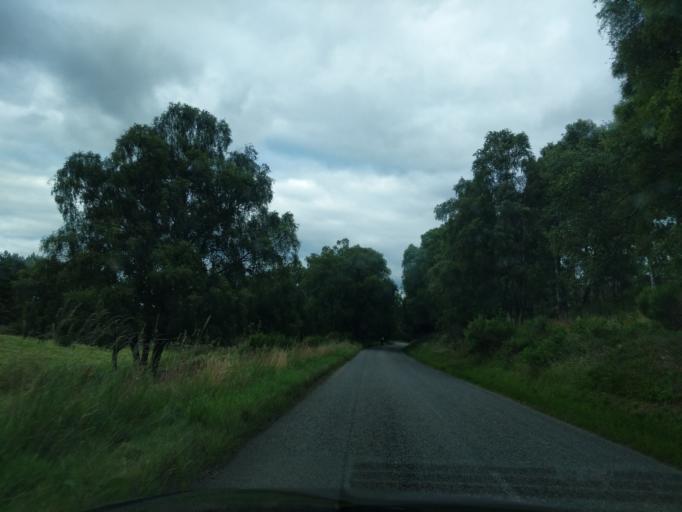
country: GB
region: Scotland
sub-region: Aberdeenshire
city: Aboyne
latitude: 57.0698
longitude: -2.8262
